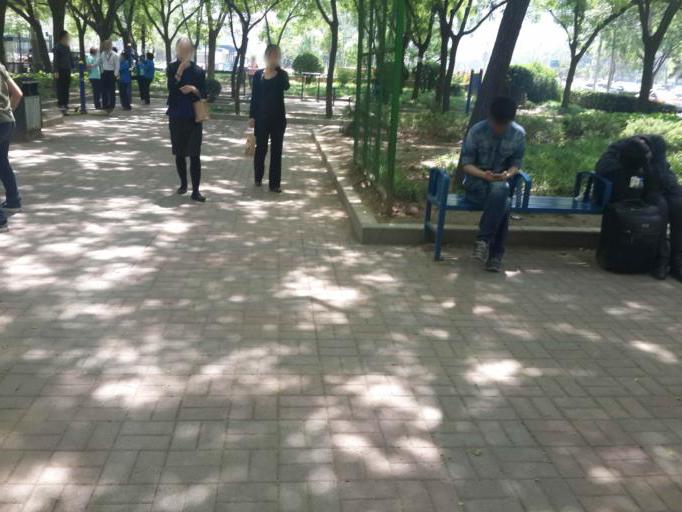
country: CN
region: Beijing
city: Chaowai
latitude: 39.9264
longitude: 116.4287
